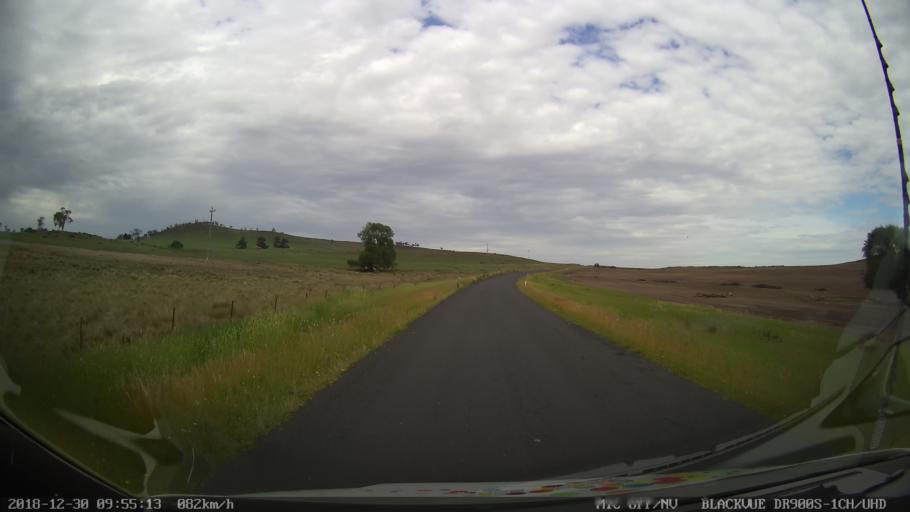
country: AU
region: New South Wales
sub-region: Cooma-Monaro
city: Cooma
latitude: -36.5202
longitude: 149.2676
